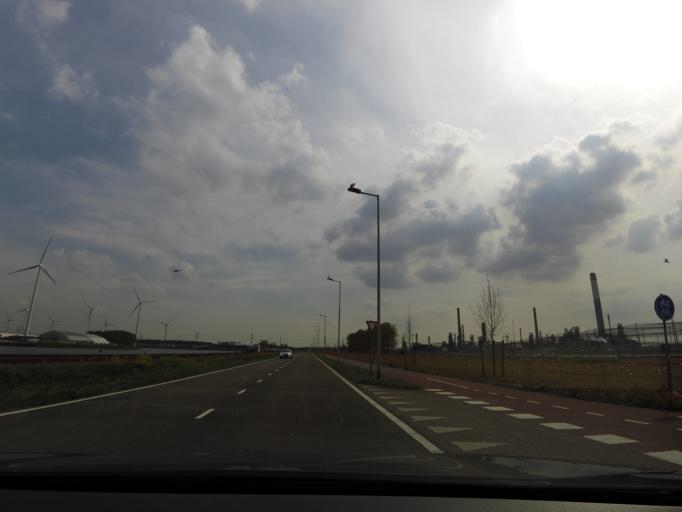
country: NL
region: South Holland
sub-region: Gemeente Rotterdam
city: Hoek van Holland
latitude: 51.9501
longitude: 4.1154
